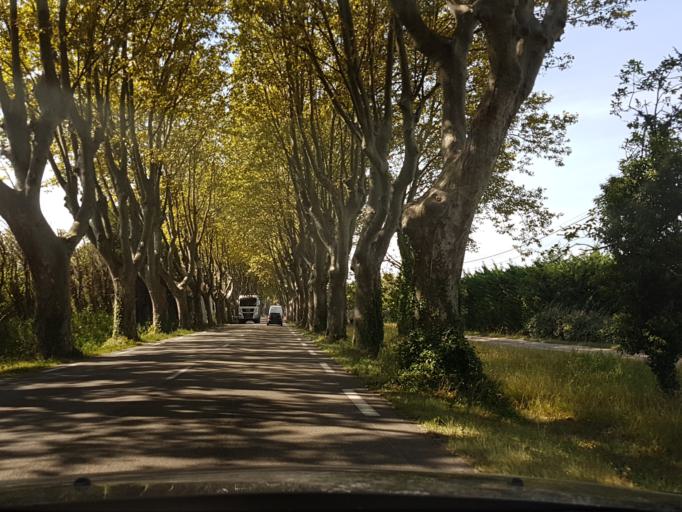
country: FR
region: Provence-Alpes-Cote d'Azur
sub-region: Departement des Bouches-du-Rhone
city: Saint-Remy-de-Provence
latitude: 43.7843
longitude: 4.8886
